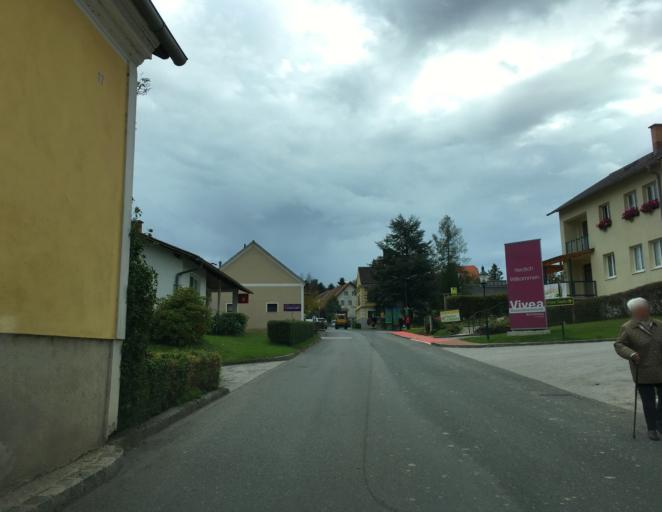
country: AT
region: Lower Austria
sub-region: Politischer Bezirk Wiener Neustadt
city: Bad Schonau
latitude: 47.4965
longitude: 16.2340
